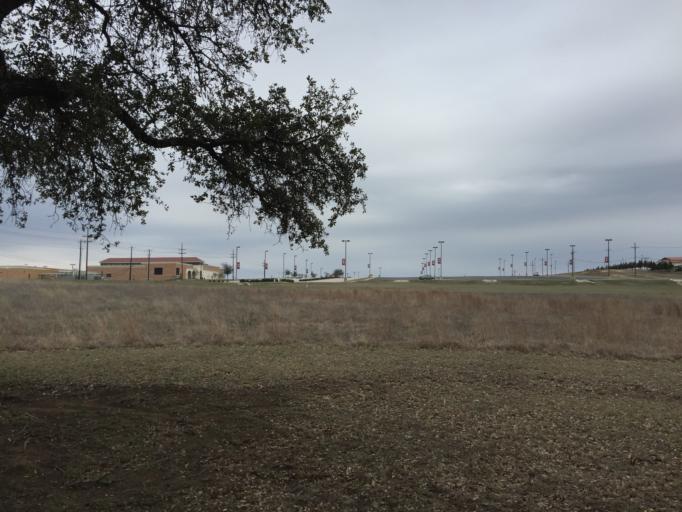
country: US
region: Texas
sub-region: Bell County
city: Fort Hood
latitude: 31.1172
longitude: -97.8117
